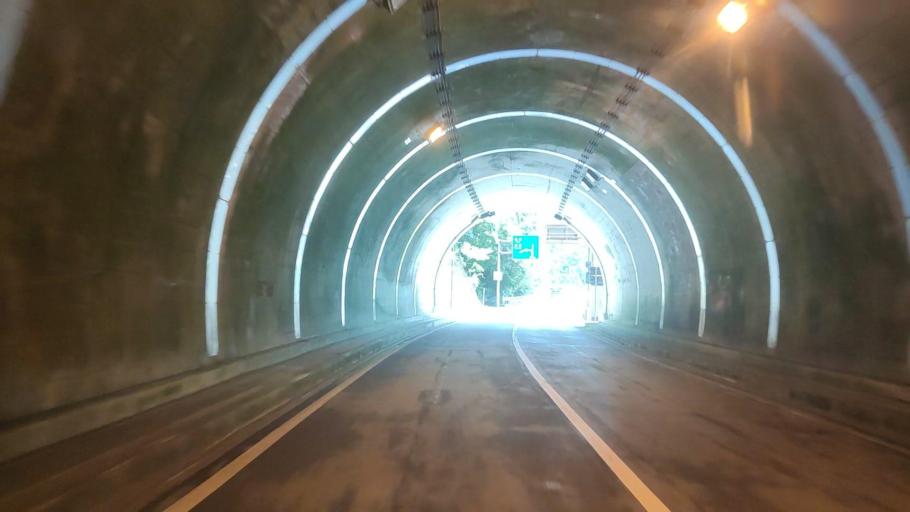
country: JP
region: Wakayama
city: Shingu
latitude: 33.9210
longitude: 135.9154
